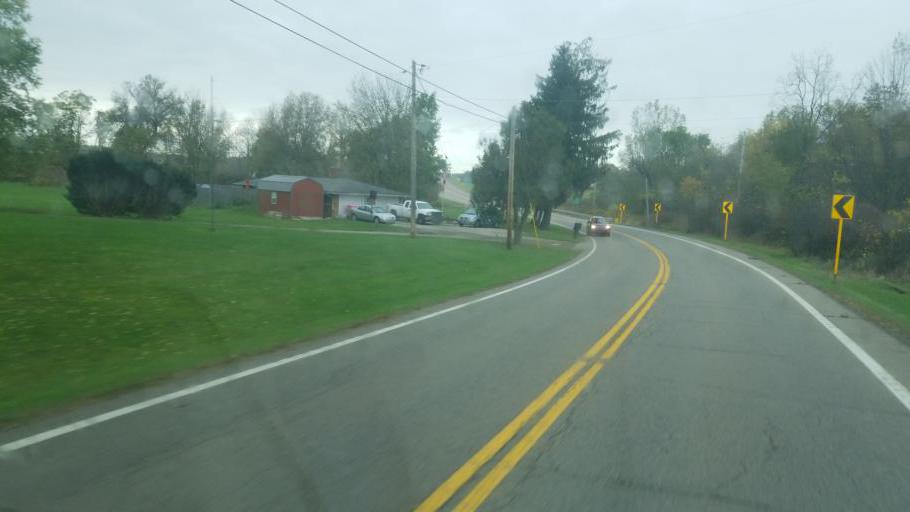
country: US
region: Ohio
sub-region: Richland County
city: Lincoln Heights
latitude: 40.7339
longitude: -82.4532
